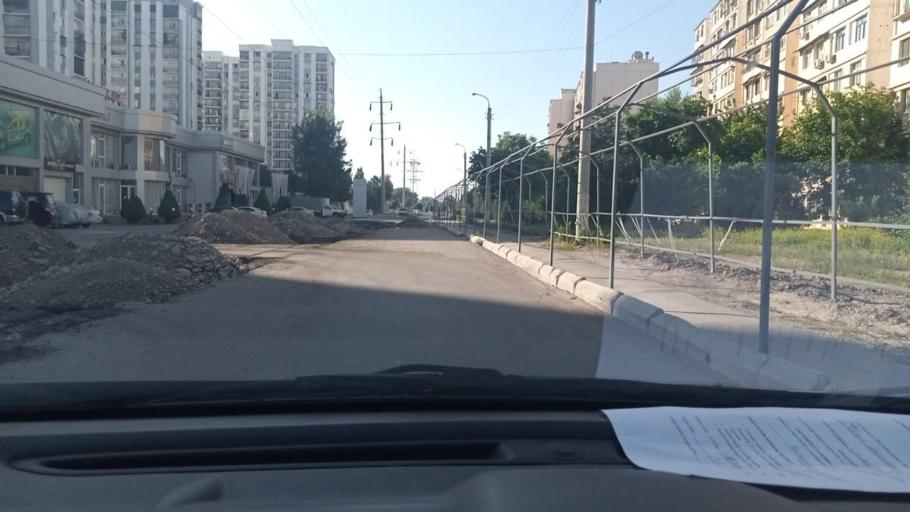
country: UZ
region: Toshkent
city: Salor
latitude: 41.3226
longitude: 69.3588
